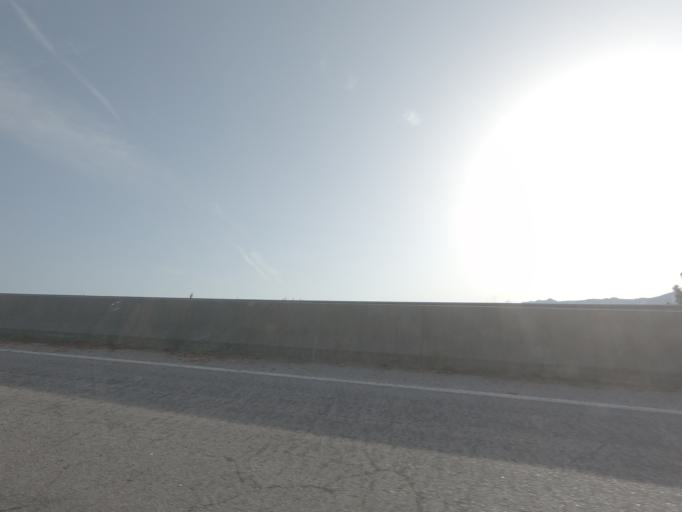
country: PT
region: Vila Real
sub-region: Sabrosa
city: Sabrosa
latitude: 41.2849
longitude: -7.4738
